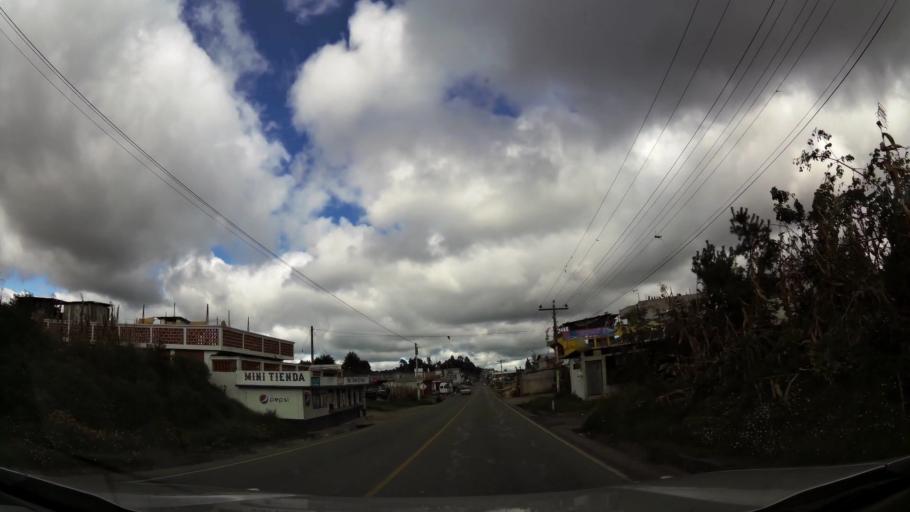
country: GT
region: Quiche
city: Chichicastenango
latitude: 14.8754
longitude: -91.1377
